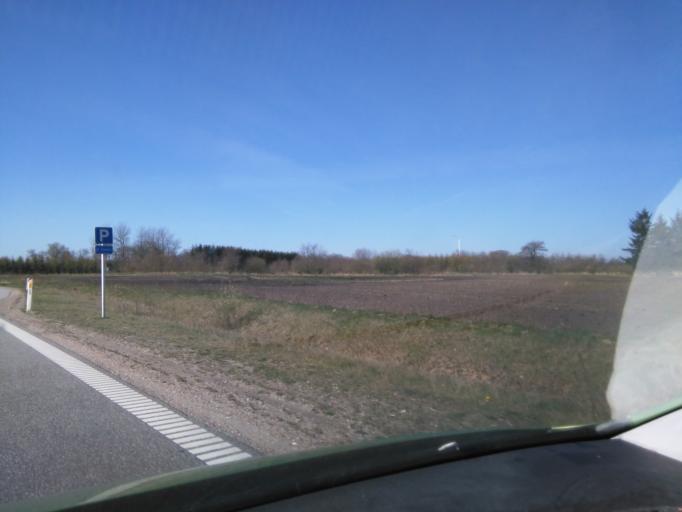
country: DK
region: South Denmark
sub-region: Vejle Kommune
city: Give
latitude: 55.8363
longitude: 9.2667
